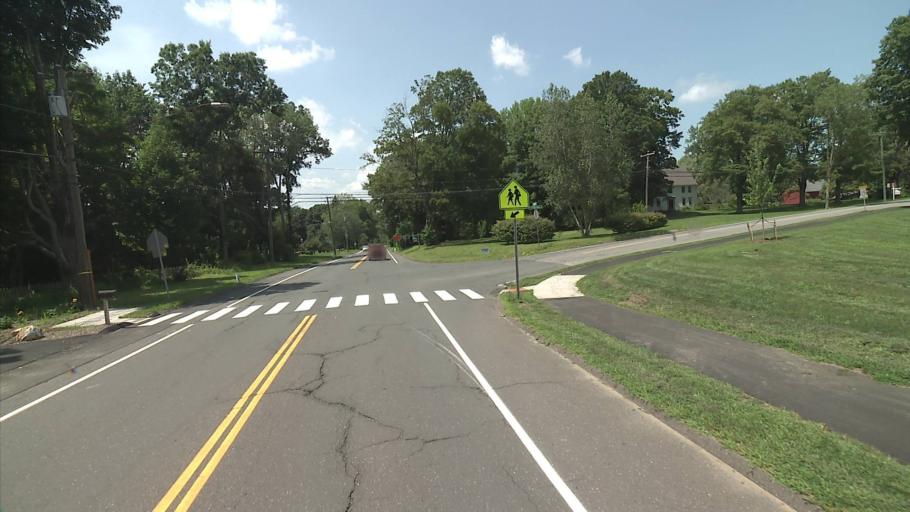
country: US
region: Connecticut
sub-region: Tolland County
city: South Coventry
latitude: 41.7813
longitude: -72.3145
